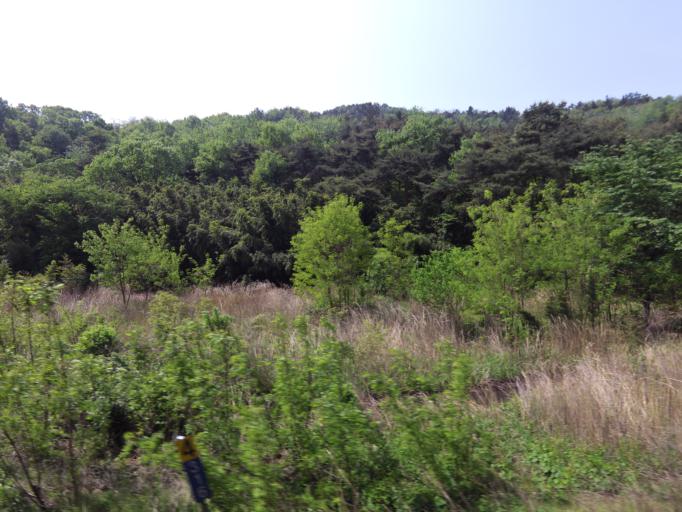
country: KR
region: Daegu
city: Daegu
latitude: 35.8899
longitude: 128.5182
